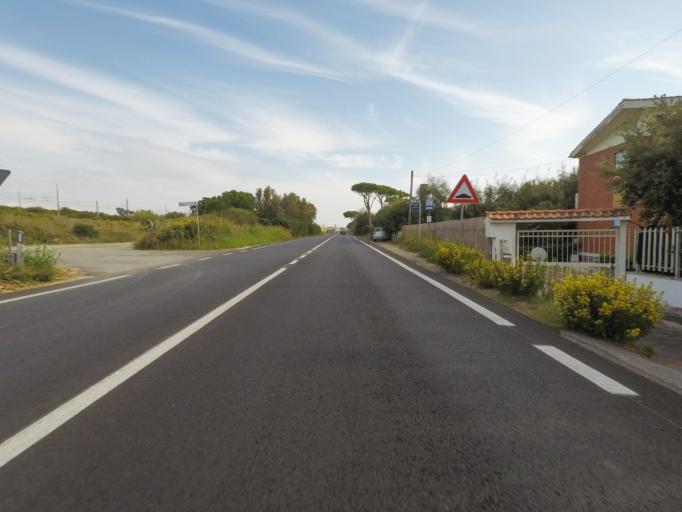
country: IT
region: Latium
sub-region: Citta metropolitana di Roma Capitale
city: Santa Marinella
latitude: 42.0468
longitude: 11.8232
